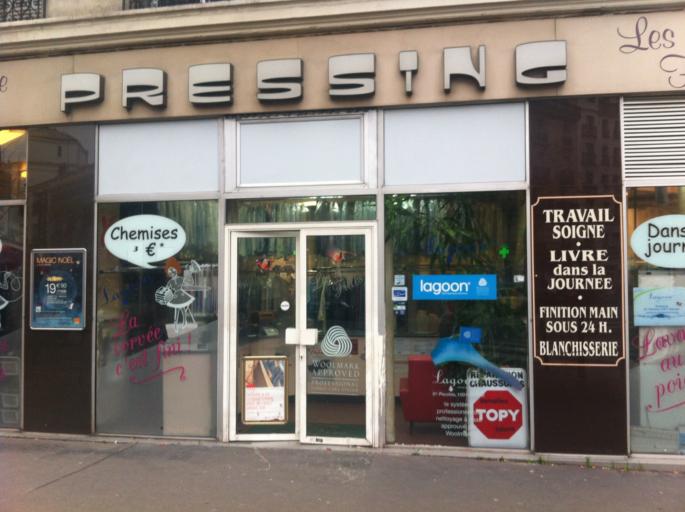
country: FR
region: Ile-de-France
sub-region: Paris
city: Paris
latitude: 48.8495
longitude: 2.3743
